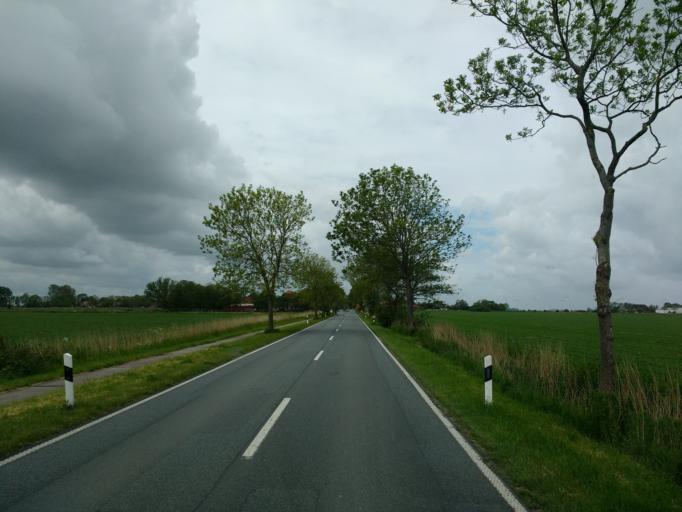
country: DE
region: Lower Saxony
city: Schillig
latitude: 53.6848
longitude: 7.9969
